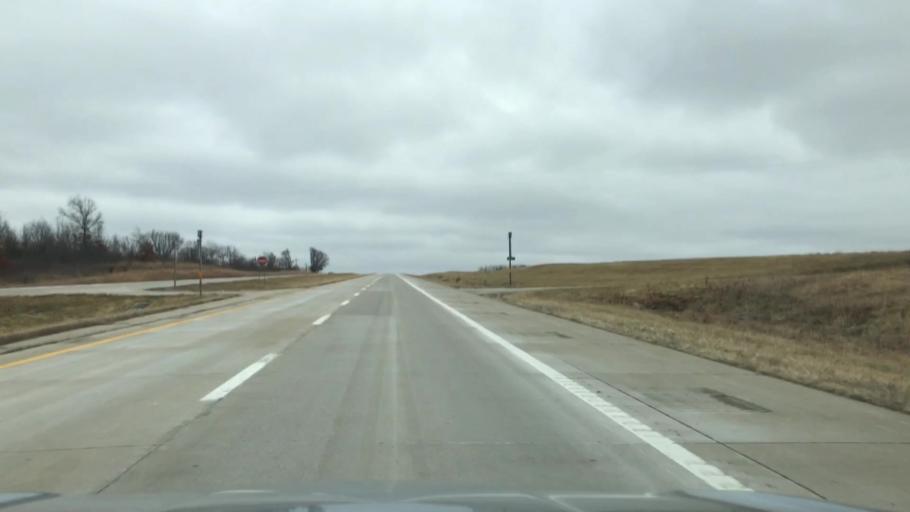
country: US
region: Missouri
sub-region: Livingston County
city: Chillicothe
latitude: 39.7381
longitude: -93.6951
